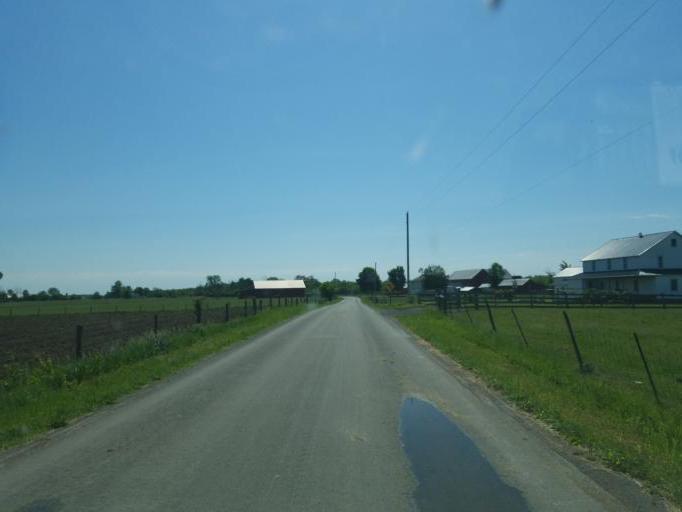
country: US
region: Ohio
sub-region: Hardin County
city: Kenton
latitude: 40.5974
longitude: -83.5512
